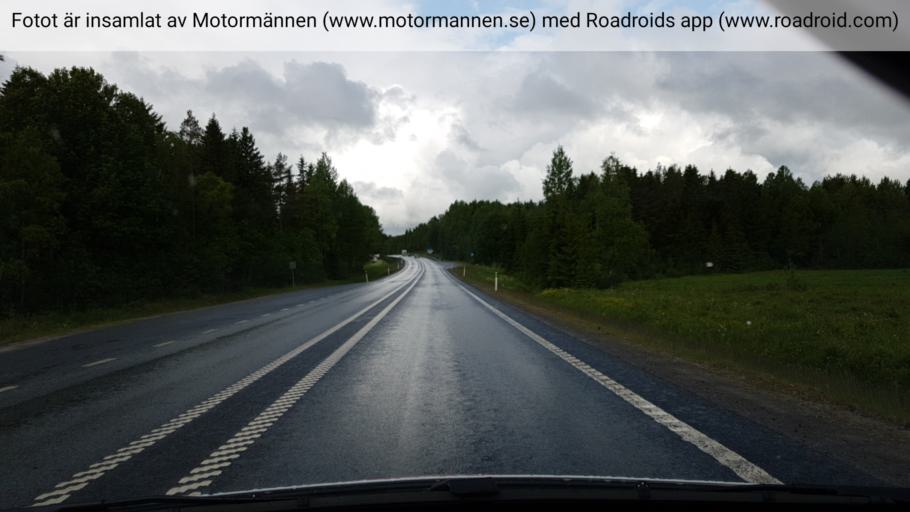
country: SE
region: Vaesterbotten
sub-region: Vannas Kommun
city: Vannasby
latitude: 63.9208
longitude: 19.8198
